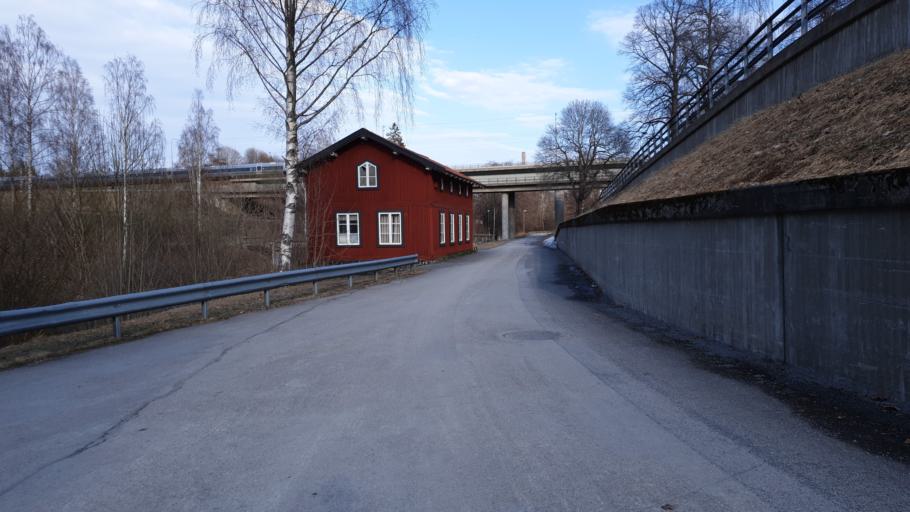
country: SE
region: Gaevleborg
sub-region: Hudiksvalls Kommun
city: Iggesund
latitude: 61.6389
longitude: 17.0756
